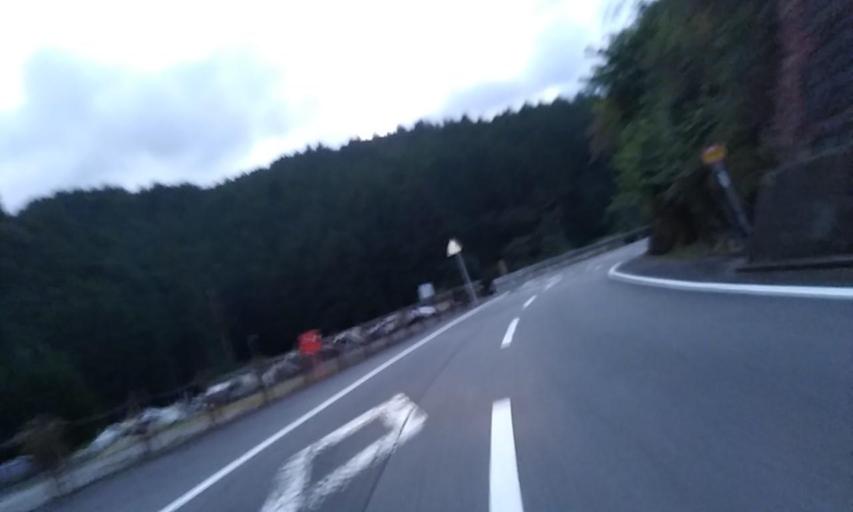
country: JP
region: Wakayama
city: Shingu
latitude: 33.7328
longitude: 135.9300
